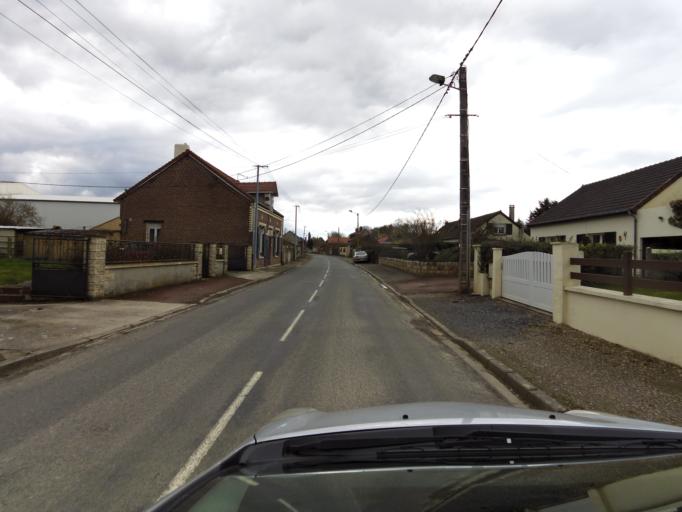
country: FR
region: Picardie
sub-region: Departement de la Somme
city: Roye
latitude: 49.7400
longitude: 2.7783
